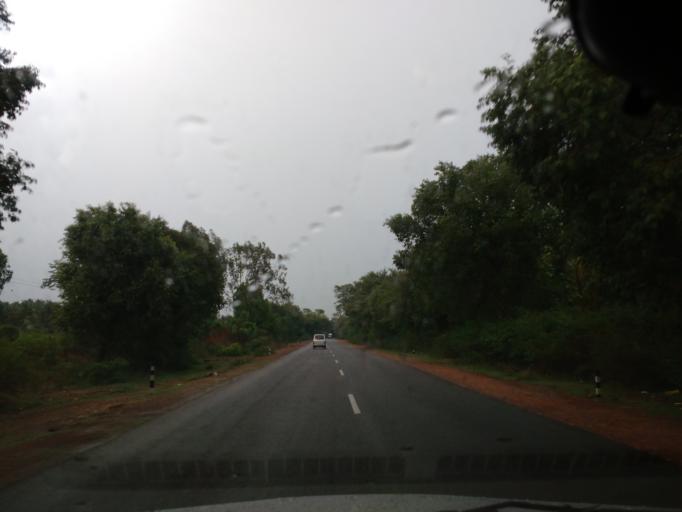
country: IN
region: Karnataka
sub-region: Tumkur
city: Chiknayakanhalli
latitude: 13.3045
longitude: 76.6000
